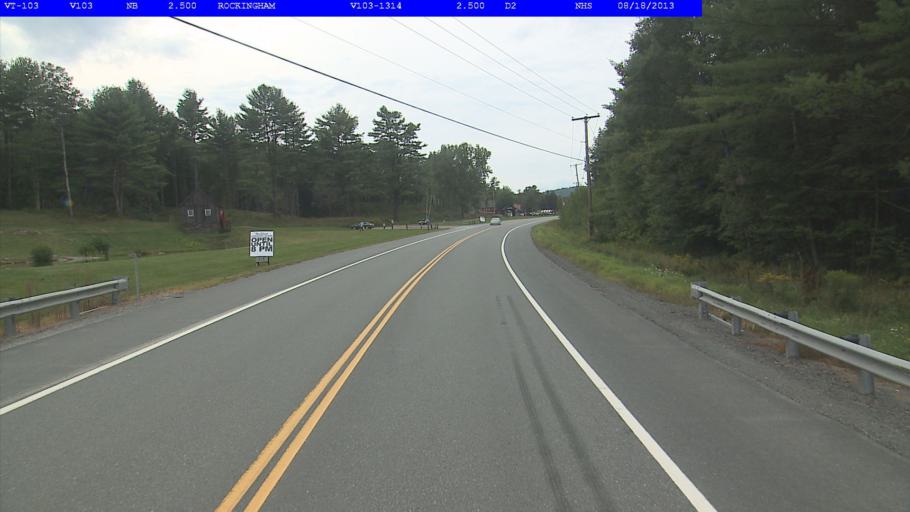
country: US
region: Vermont
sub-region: Windham County
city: Rockingham
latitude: 43.1955
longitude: -72.5015
